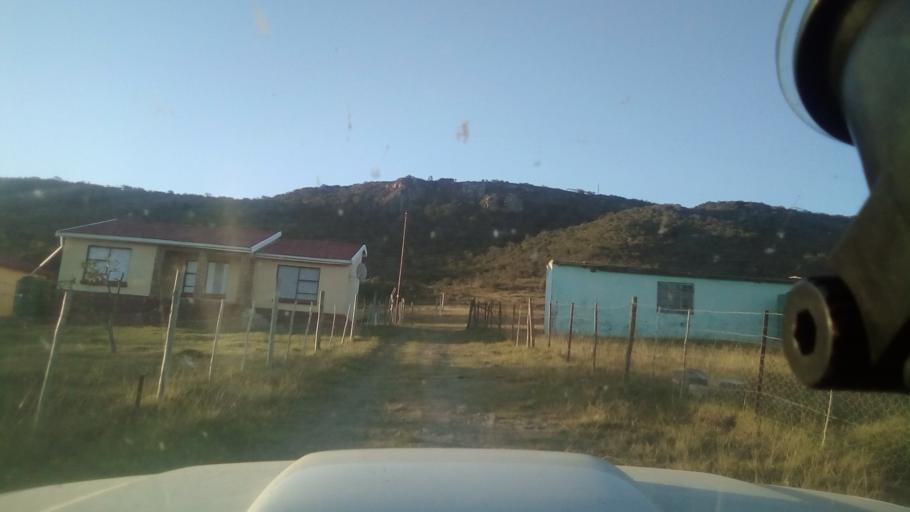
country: ZA
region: Eastern Cape
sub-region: Buffalo City Metropolitan Municipality
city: Bhisho
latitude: -32.7335
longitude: 27.3779
